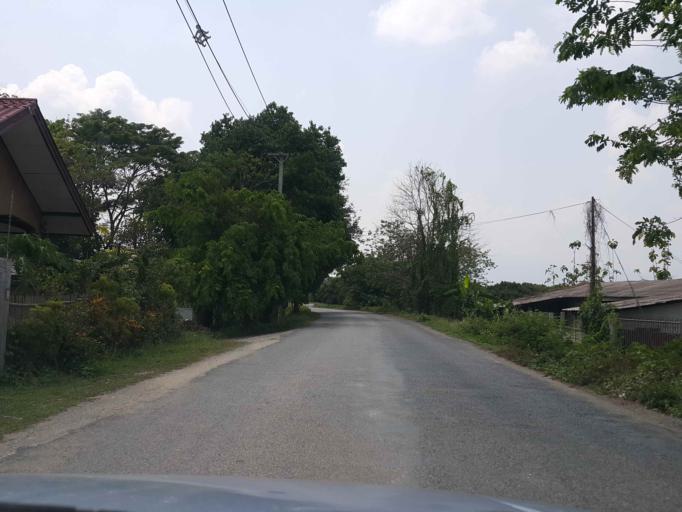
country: TH
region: Chiang Mai
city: Saraphi
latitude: 18.6762
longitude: 99.0075
